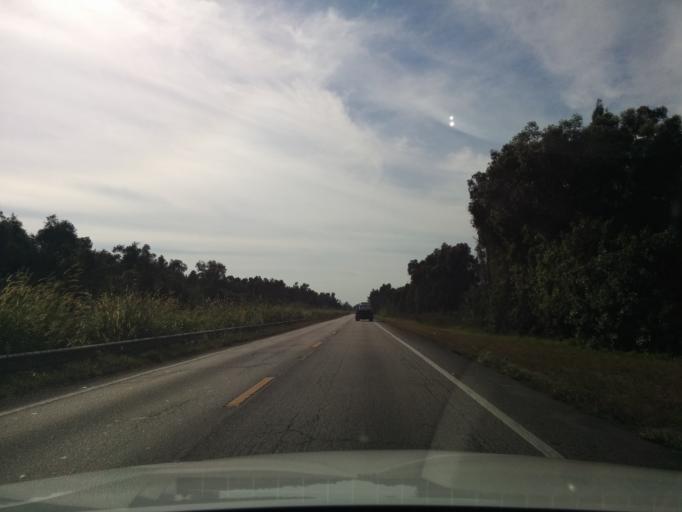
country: US
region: Florida
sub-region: Miami-Dade County
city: Kendall West
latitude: 25.7208
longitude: -80.4798
